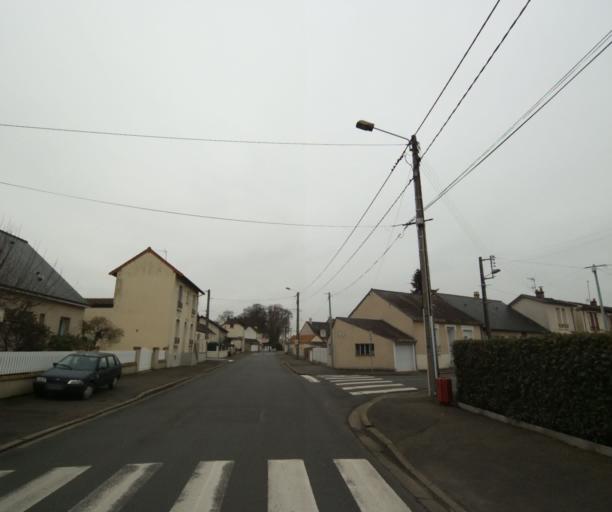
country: FR
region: Pays de la Loire
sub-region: Departement de la Sarthe
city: Le Mans
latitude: 47.9841
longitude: 0.1922
